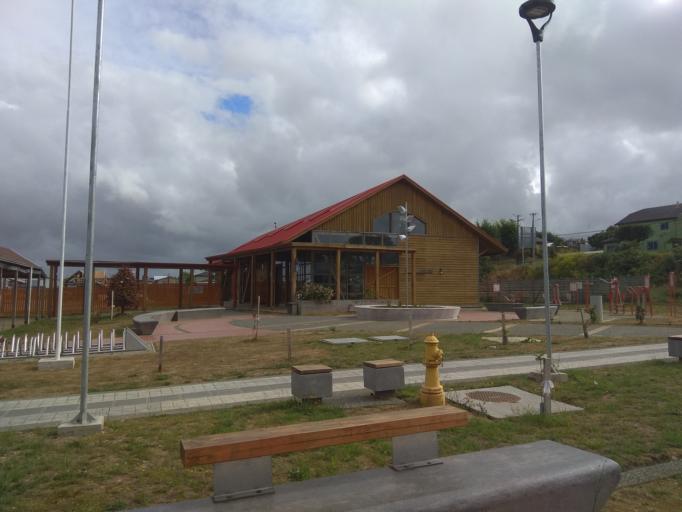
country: CL
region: Los Lagos
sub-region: Provincia de Llanquihue
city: Puerto Varas
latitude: -41.3953
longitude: -73.4646
